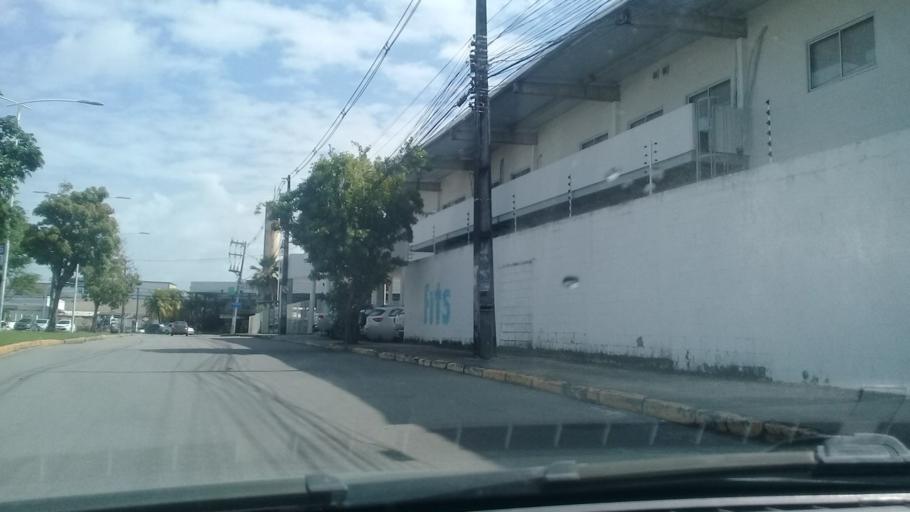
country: BR
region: Pernambuco
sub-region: Jaboatao Dos Guararapes
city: Jaboatao
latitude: -8.1679
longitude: -34.9205
